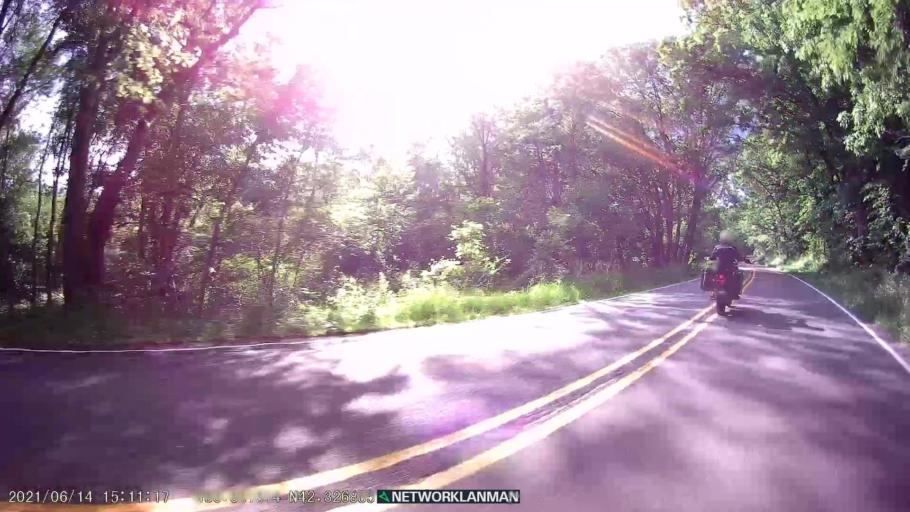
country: US
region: Michigan
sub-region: Washtenaw County
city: Dexter
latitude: 42.3270
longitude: -83.8516
